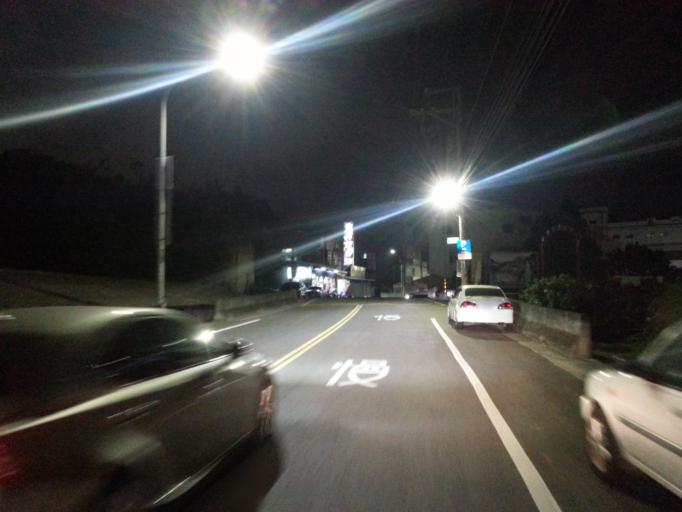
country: TW
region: Taiwan
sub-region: Hsinchu
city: Hsinchu
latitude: 24.7842
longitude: 120.9317
